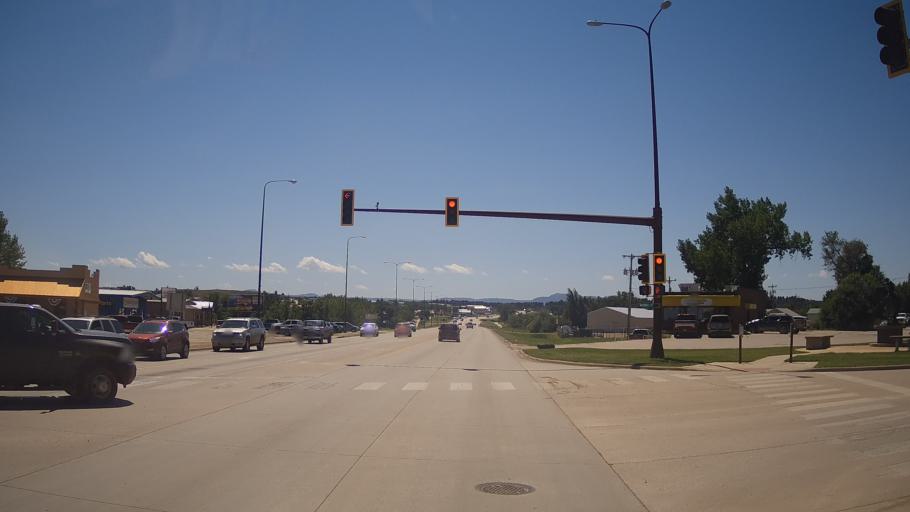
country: US
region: South Dakota
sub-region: Butte County
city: Belle Fourche
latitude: 44.6628
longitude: -103.8544
